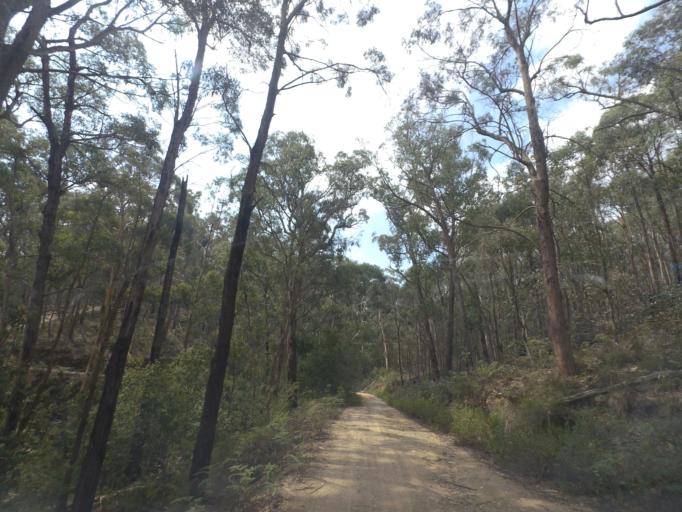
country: AU
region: Victoria
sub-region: Moorabool
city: Bacchus Marsh
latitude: -37.4605
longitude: 144.3817
